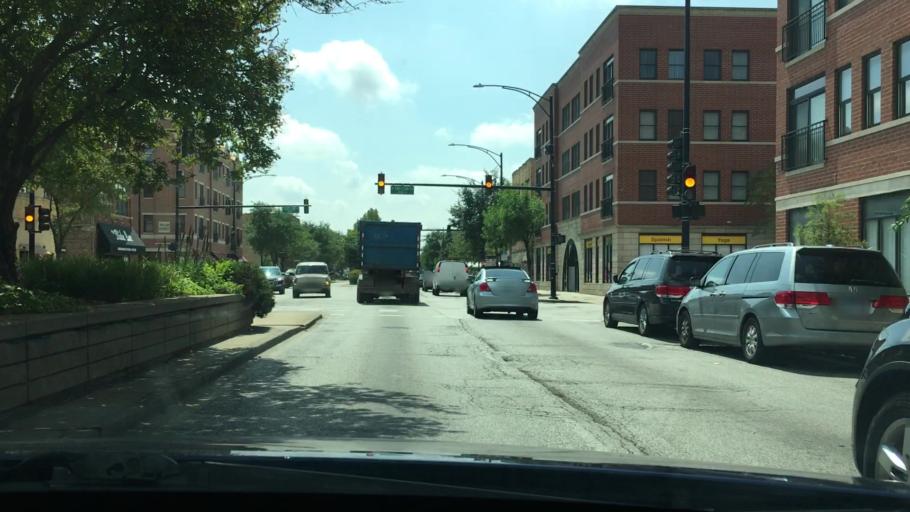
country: US
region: Illinois
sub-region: Cook County
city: Chicago
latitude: 41.8697
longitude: -87.6862
